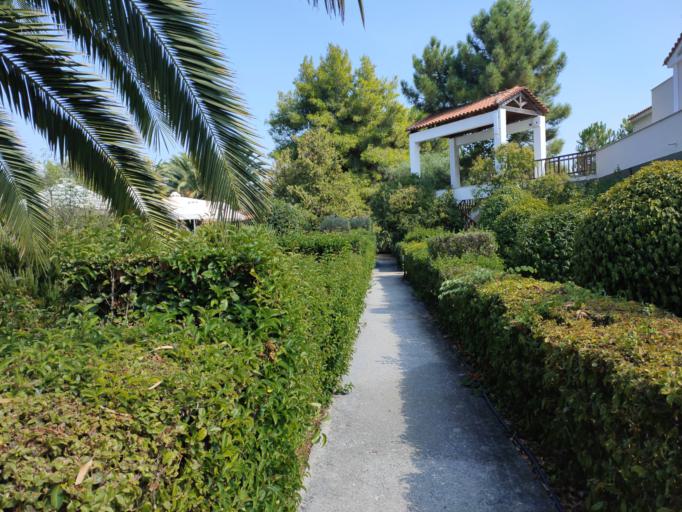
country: GR
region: North Aegean
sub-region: Nomos Lesvou
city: Kalloni
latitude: 39.2092
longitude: 26.2059
